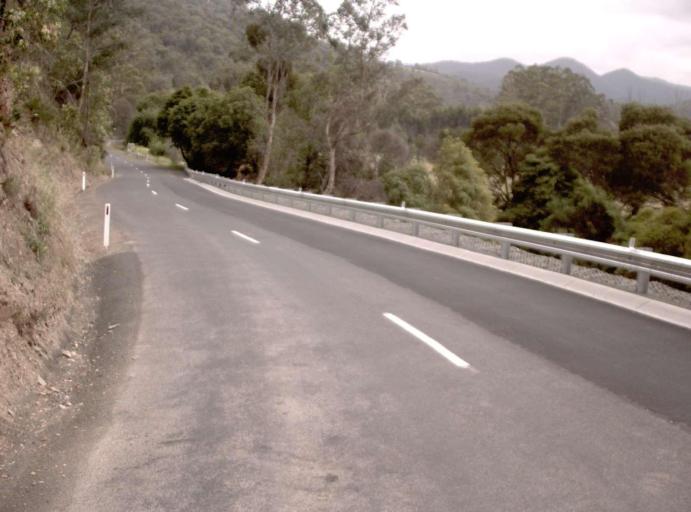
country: AU
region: Victoria
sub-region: Wellington
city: Heyfield
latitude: -37.8049
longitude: 146.6719
